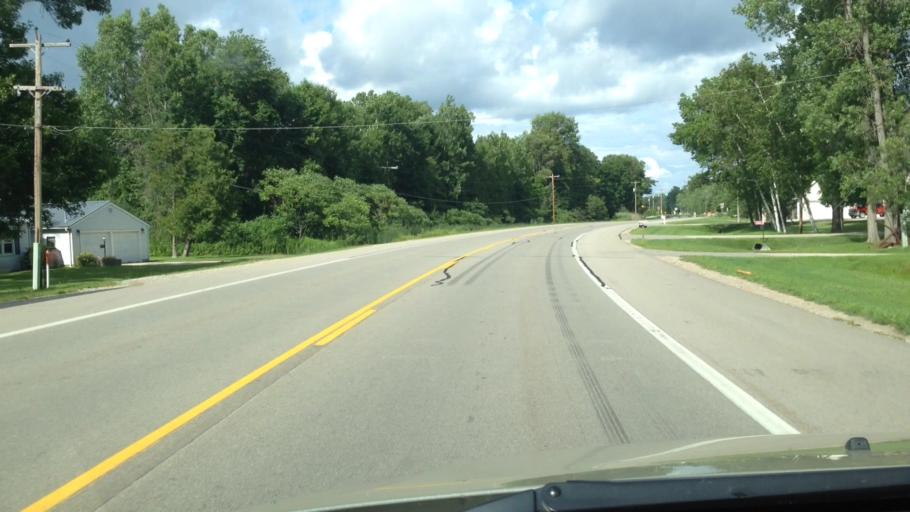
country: US
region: Michigan
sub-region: Menominee County
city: Menominee
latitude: 45.1505
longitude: -87.6016
